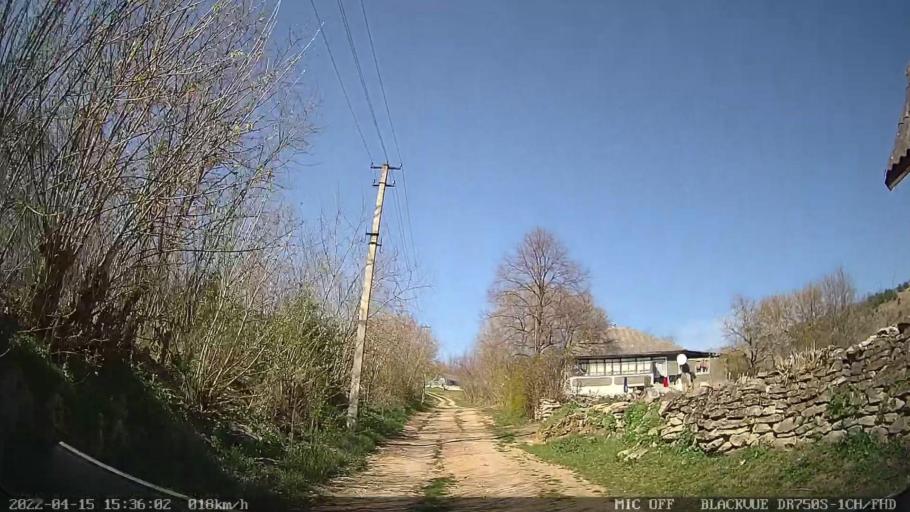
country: MD
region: Raionul Ocnita
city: Otaci
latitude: 48.3472
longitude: 27.9311
